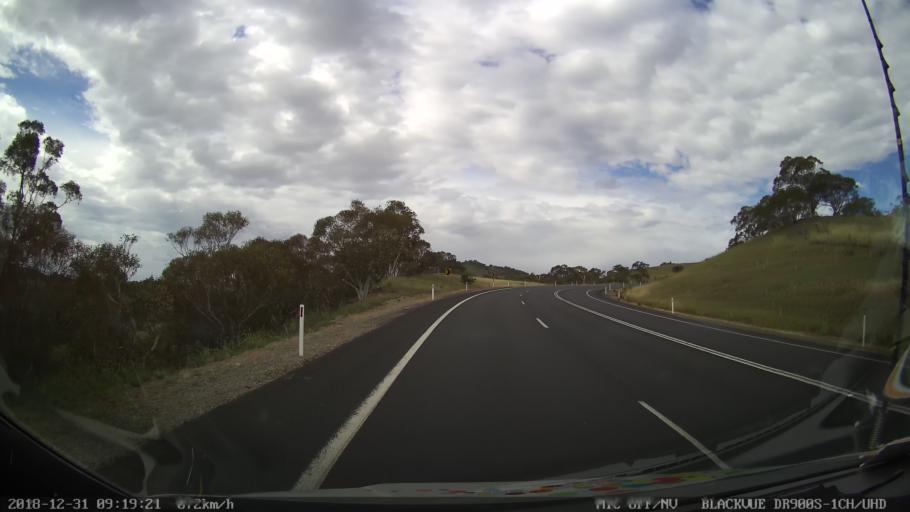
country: AU
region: New South Wales
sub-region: Snowy River
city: Jindabyne
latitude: -36.4147
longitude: 148.5864
